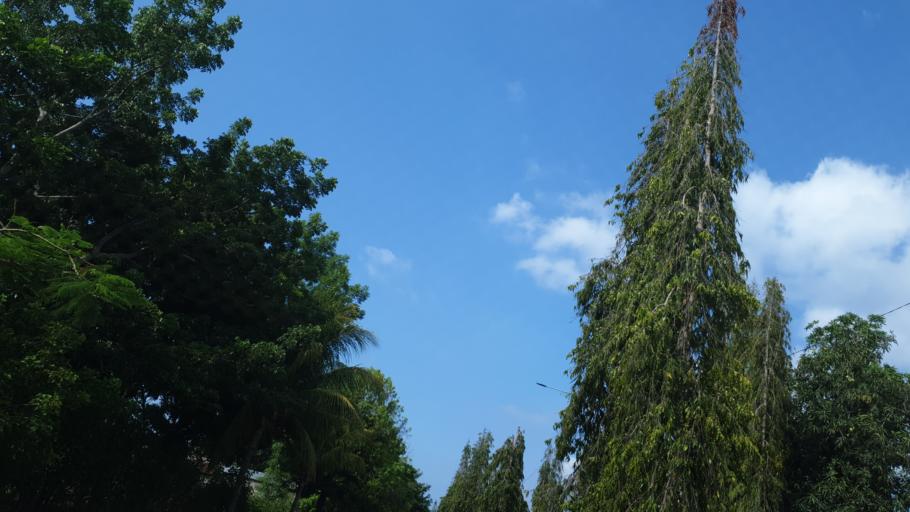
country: ID
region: East Nusa Tenggara
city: Waioti
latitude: -8.6308
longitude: 122.2366
